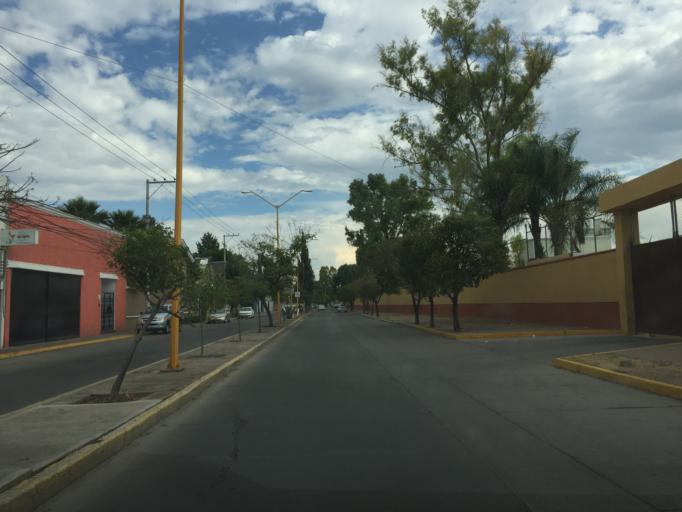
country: MX
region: Aguascalientes
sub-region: Jesus Maria
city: El Llano
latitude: 21.9213
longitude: -102.3044
